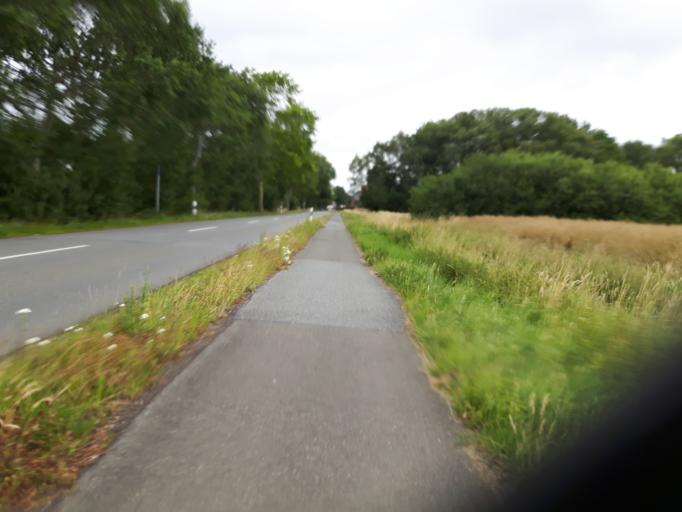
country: DE
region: Lower Saxony
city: Stuhr
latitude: 53.0099
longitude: 8.7687
